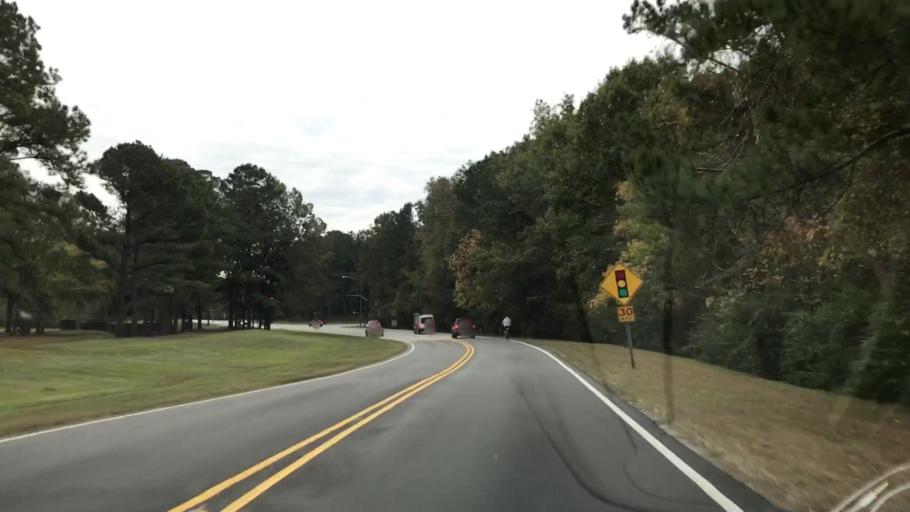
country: US
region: South Carolina
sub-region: Berkeley County
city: Goose Creek
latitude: 33.0158
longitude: -80.0660
